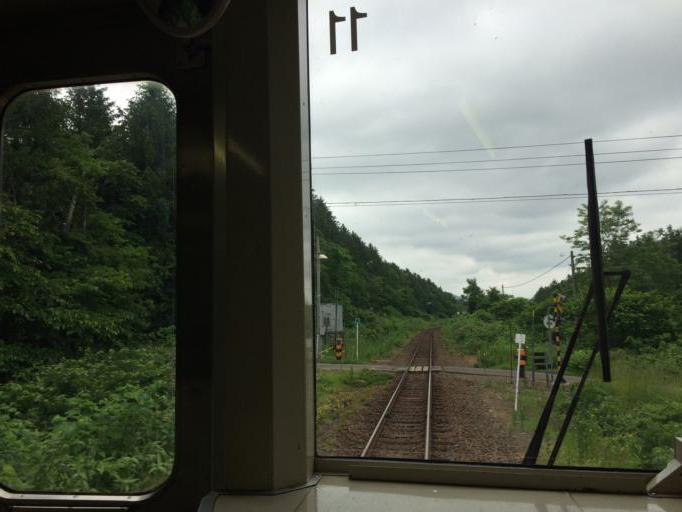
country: JP
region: Hokkaido
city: Yoichi
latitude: 43.0704
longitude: 140.7033
